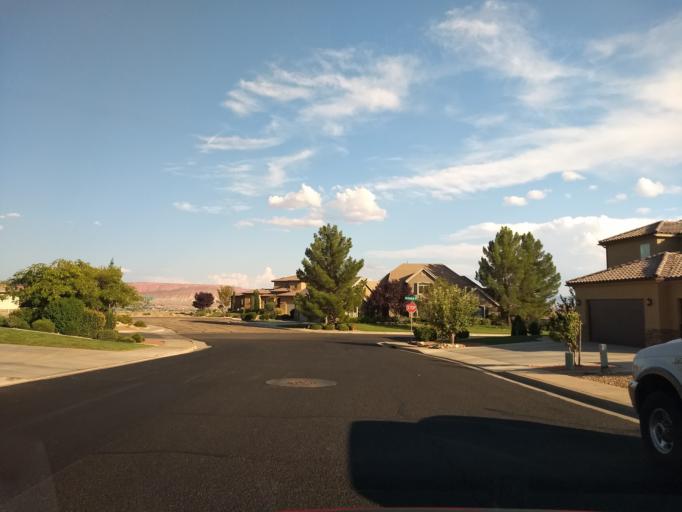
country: US
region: Utah
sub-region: Washington County
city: Saint George
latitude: 37.1027
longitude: -113.5461
